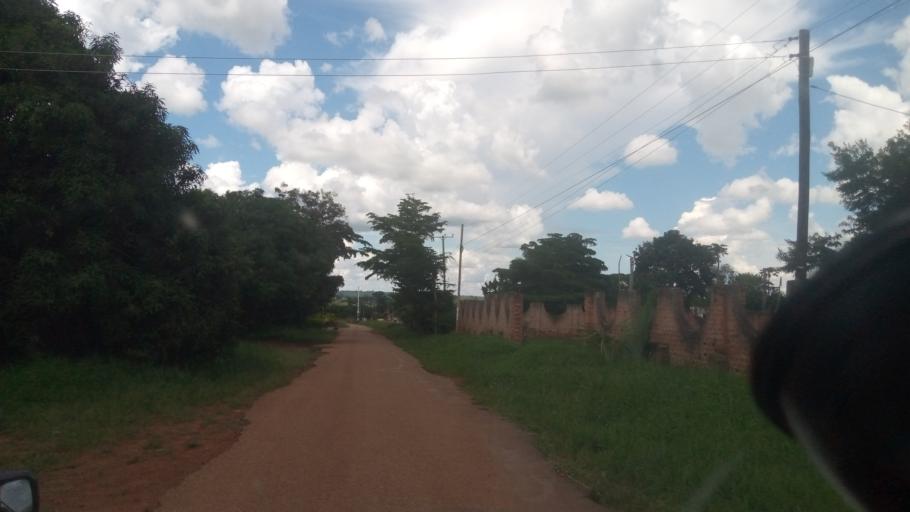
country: UG
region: Northern Region
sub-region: Lira District
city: Lira
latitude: 2.2405
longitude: 32.9065
